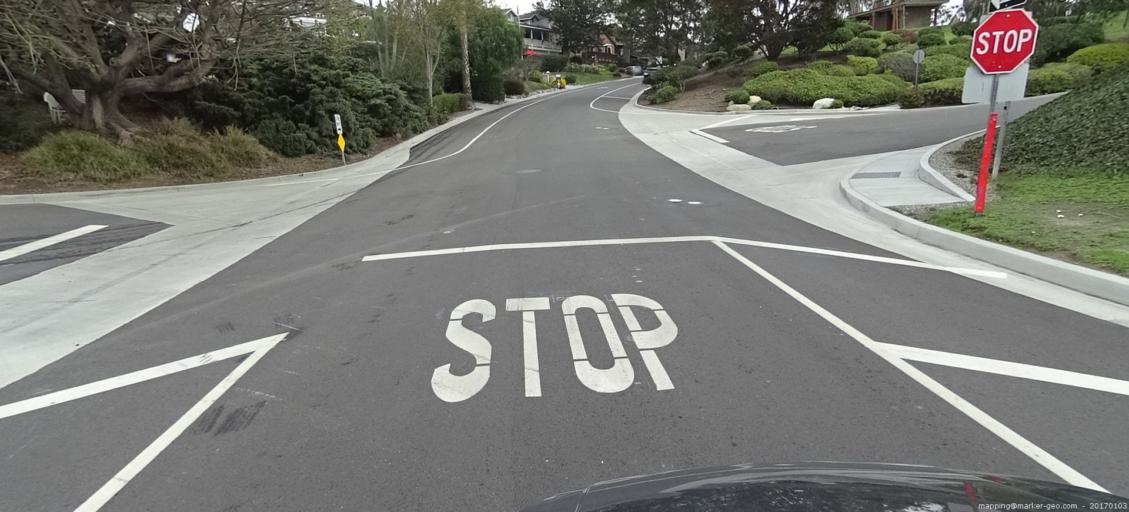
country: US
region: California
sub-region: Orange County
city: Dana Point
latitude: 33.4638
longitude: -117.6624
